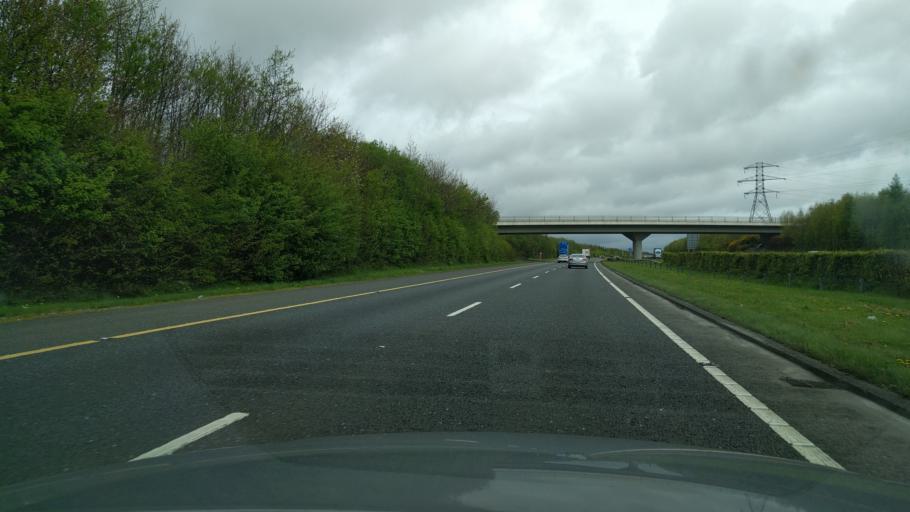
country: IE
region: Leinster
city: Balrothery
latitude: 53.5491
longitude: -6.2156
